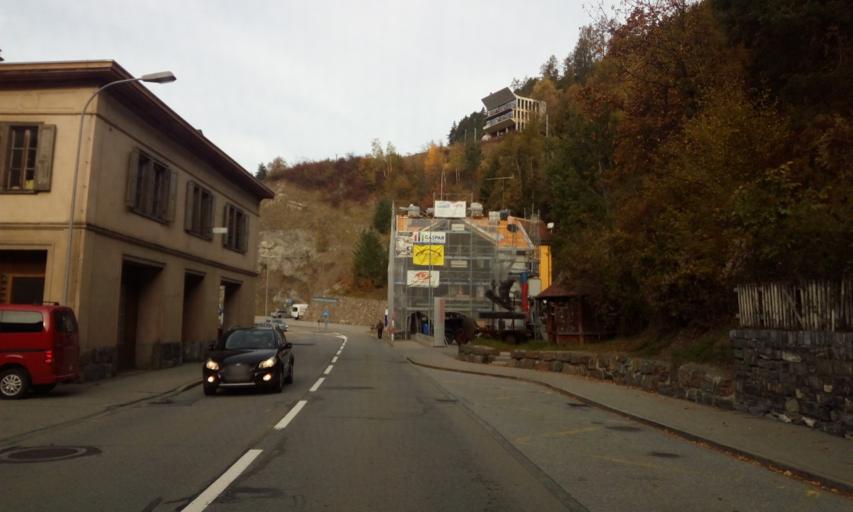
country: CH
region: Grisons
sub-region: Albula District
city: Tiefencastel
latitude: 46.6623
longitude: 9.5780
